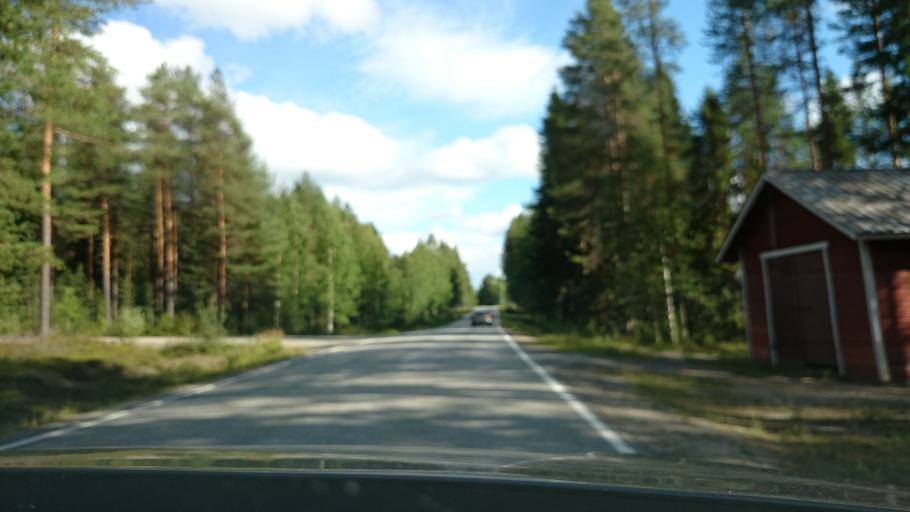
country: FI
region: Kainuu
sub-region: Kehys-Kainuu
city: Suomussalmi
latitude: 64.7483
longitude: 29.4365
